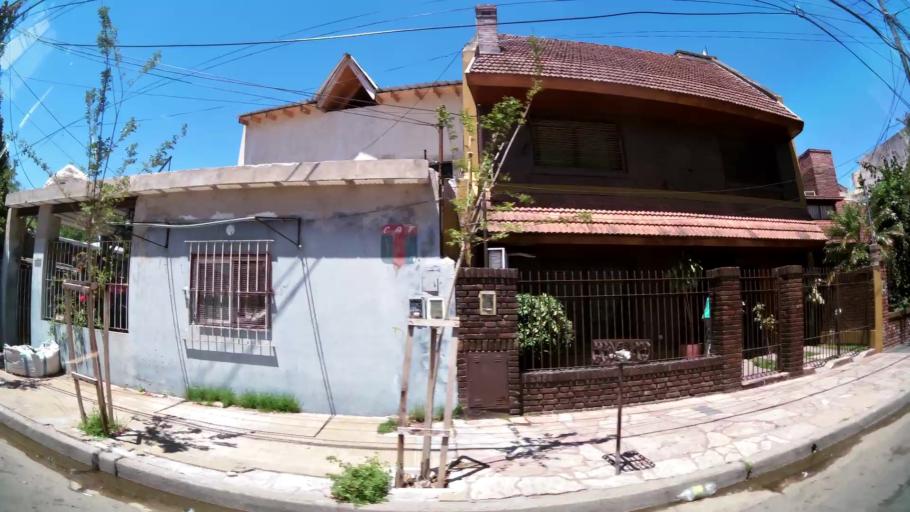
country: AR
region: Buenos Aires
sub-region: Partido de Tigre
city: Tigre
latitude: -34.4495
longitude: -58.5582
